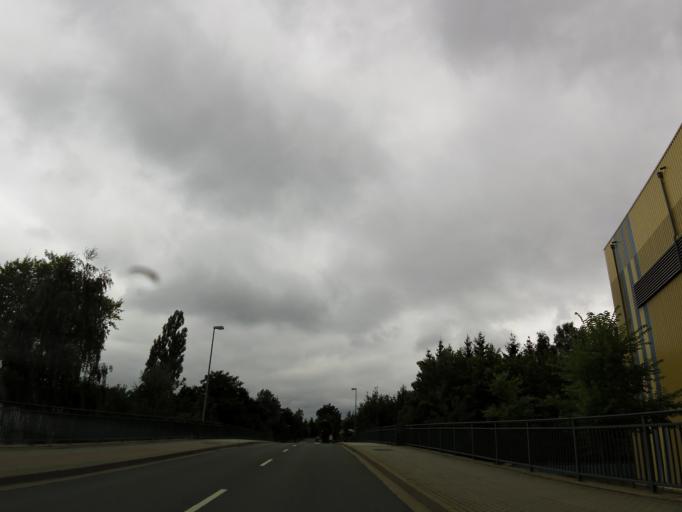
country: DE
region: Thuringia
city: Hermsdorf
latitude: 50.9005
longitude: 11.8516
